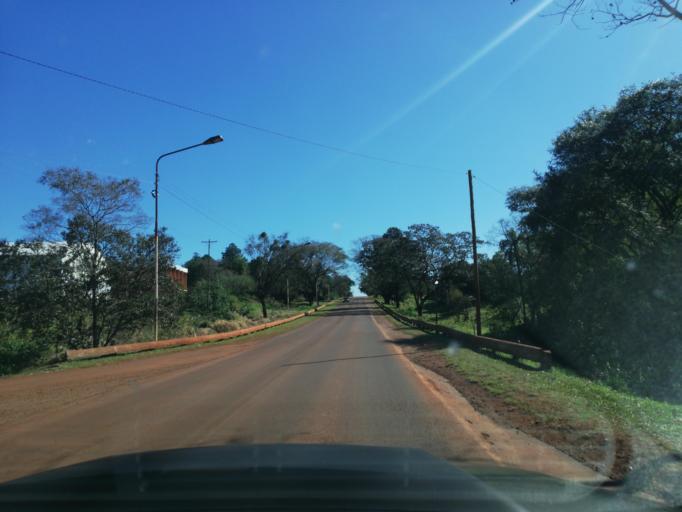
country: AR
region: Misiones
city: Aristobulo del Valle
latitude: -27.0911
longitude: -54.9005
